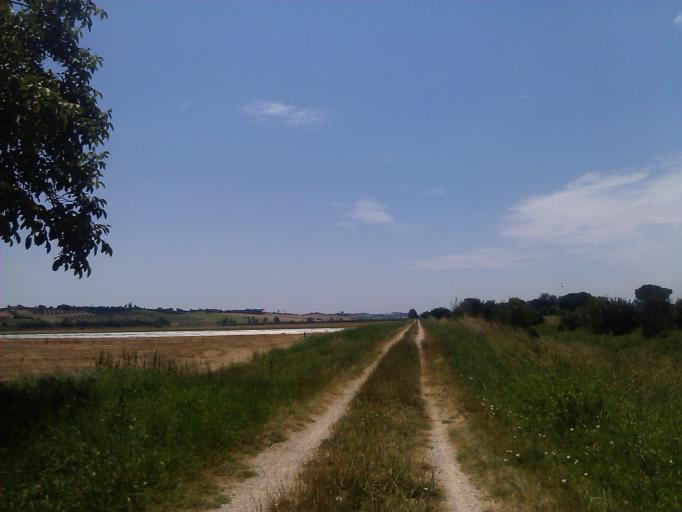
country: IT
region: Tuscany
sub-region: Province of Arezzo
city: Cesa
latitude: 43.3040
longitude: 11.8398
